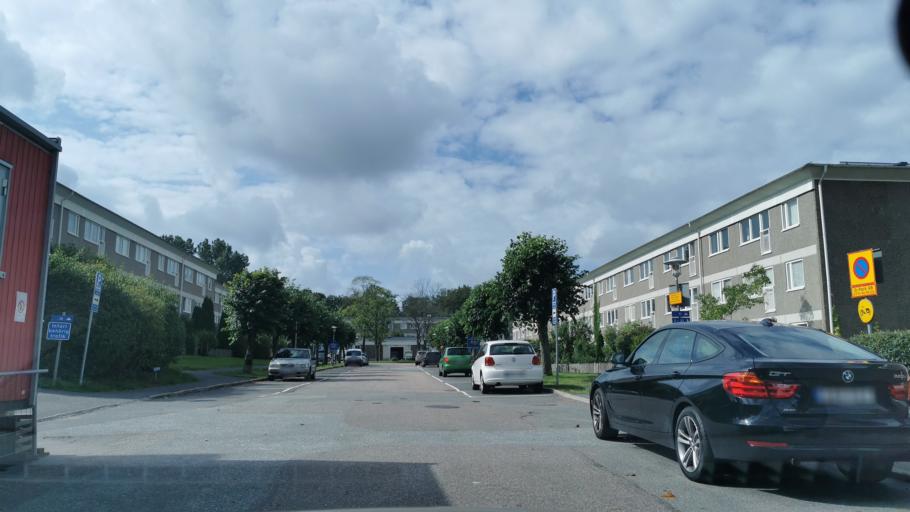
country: SE
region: Vaestra Goetaland
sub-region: Goteborg
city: Majorna
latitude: 57.6386
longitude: 11.9424
